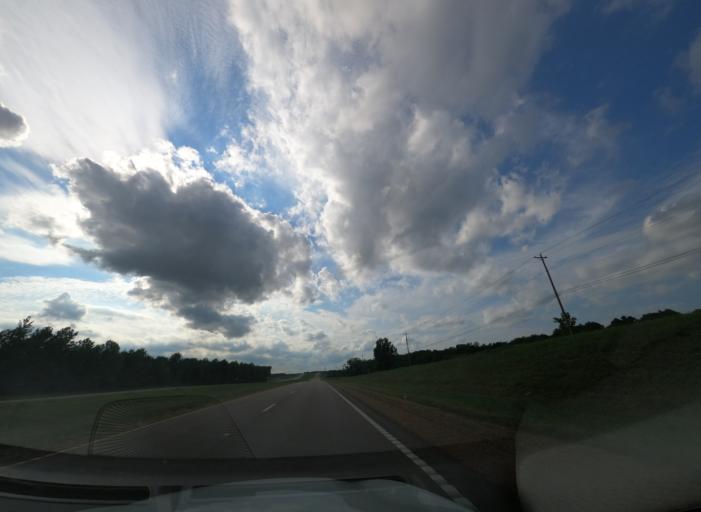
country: US
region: Tennessee
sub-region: Fayette County
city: Piperton
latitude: 34.9827
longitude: -89.5871
